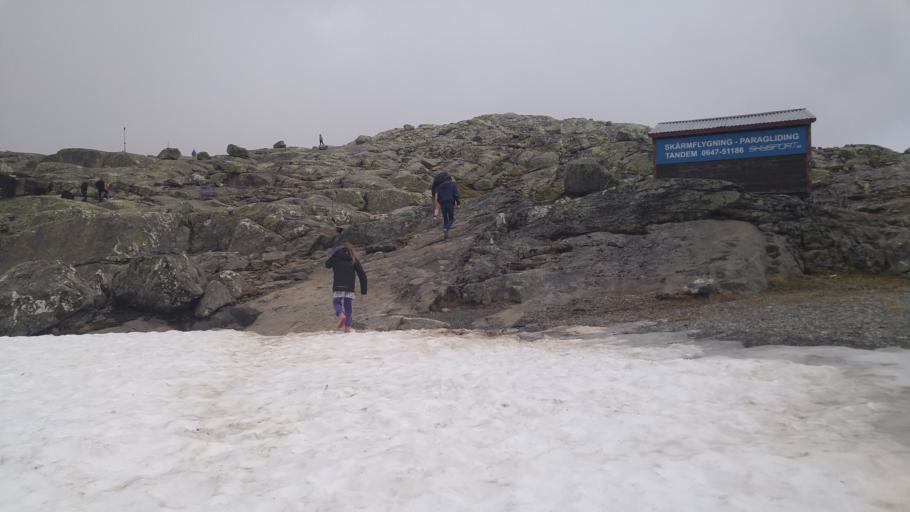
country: SE
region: Jaemtland
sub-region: Are Kommun
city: Are
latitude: 63.4276
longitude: 13.0796
